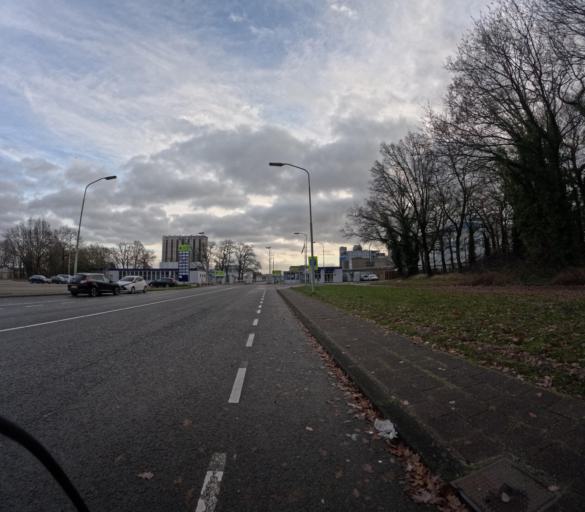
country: NL
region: Drenthe
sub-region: Gemeente Emmen
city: Emmen
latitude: 52.7757
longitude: 6.9066
